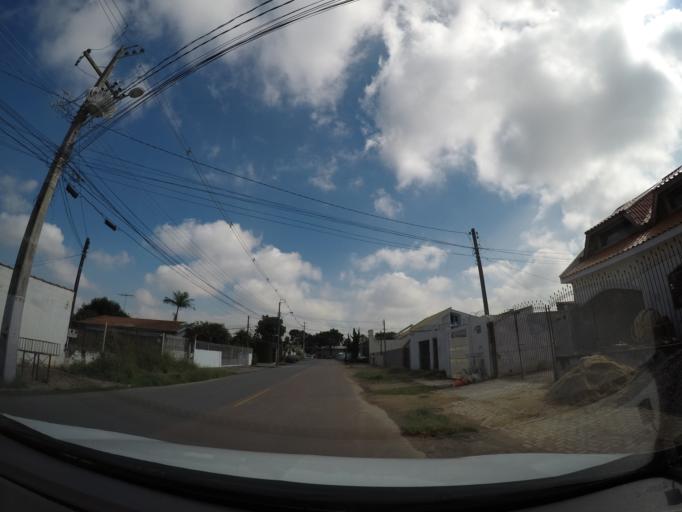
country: BR
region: Parana
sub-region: Sao Jose Dos Pinhais
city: Sao Jose dos Pinhais
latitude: -25.4959
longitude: -49.2237
